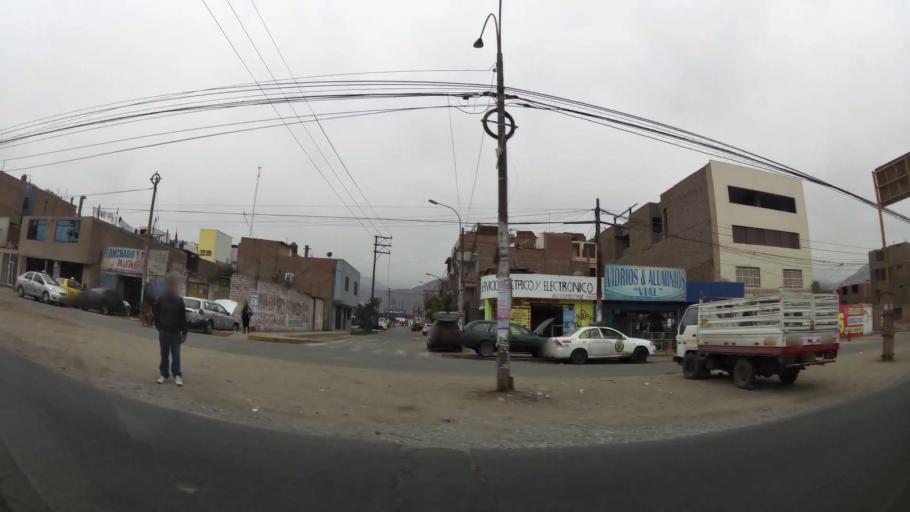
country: PE
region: Lima
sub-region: Lima
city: Independencia
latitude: -11.9491
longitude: -77.0602
